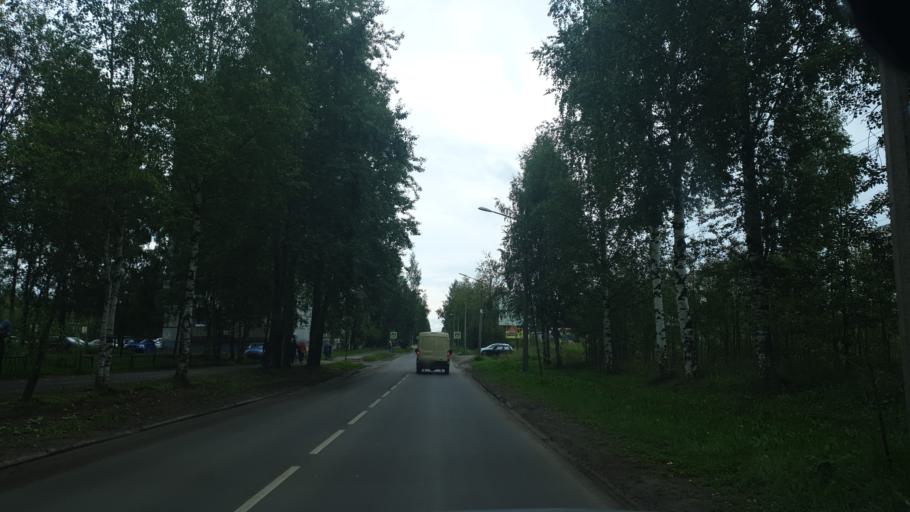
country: RU
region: Komi Republic
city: Ezhva
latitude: 61.7907
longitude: 50.7424
